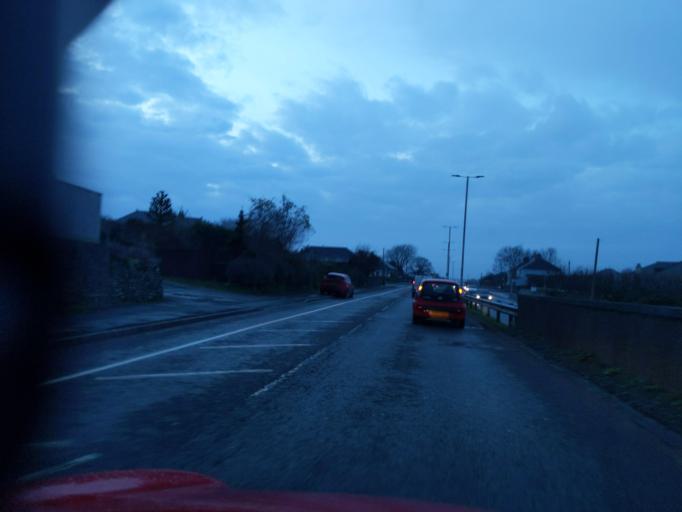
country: GB
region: England
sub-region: Plymouth
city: Plymstock
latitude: 50.3633
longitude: -4.0739
